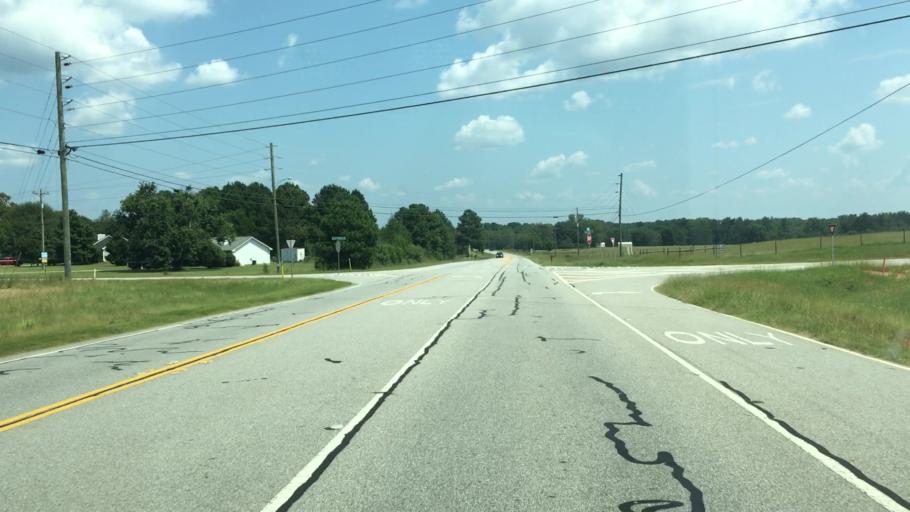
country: US
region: Georgia
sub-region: Oconee County
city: Bogart
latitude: 33.8750
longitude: -83.5262
